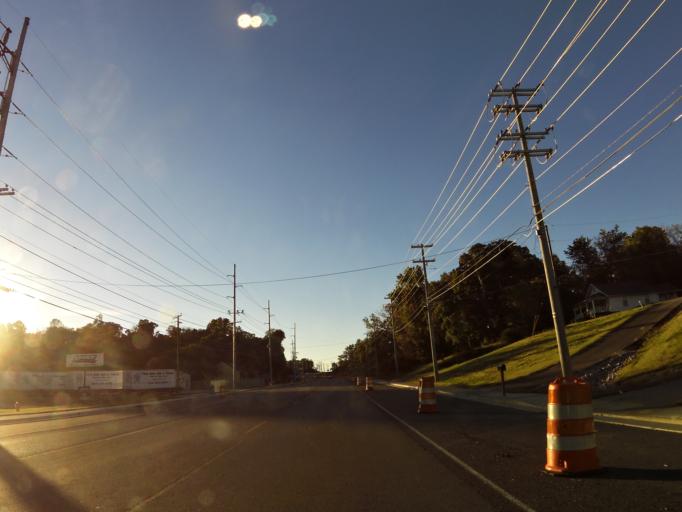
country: US
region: Tennessee
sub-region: Knox County
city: Knoxville
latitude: 35.9829
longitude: -84.0240
